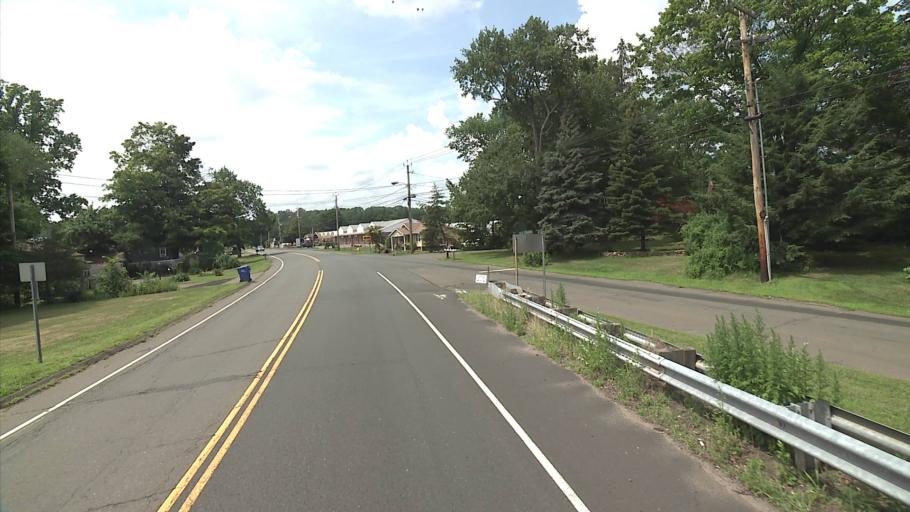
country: US
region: Connecticut
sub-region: New Haven County
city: North Haven
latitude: 41.3805
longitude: -72.8127
